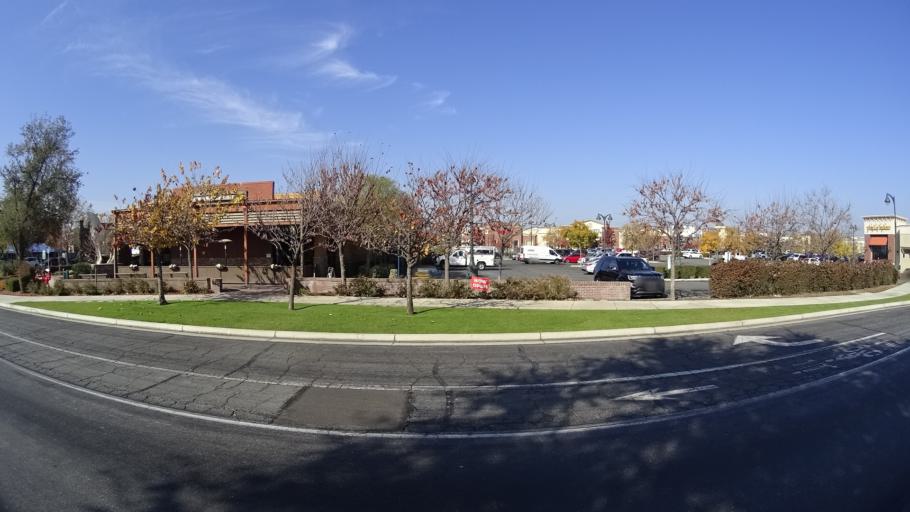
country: US
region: California
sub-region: Kern County
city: Greenacres
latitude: 35.3502
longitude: -119.1210
